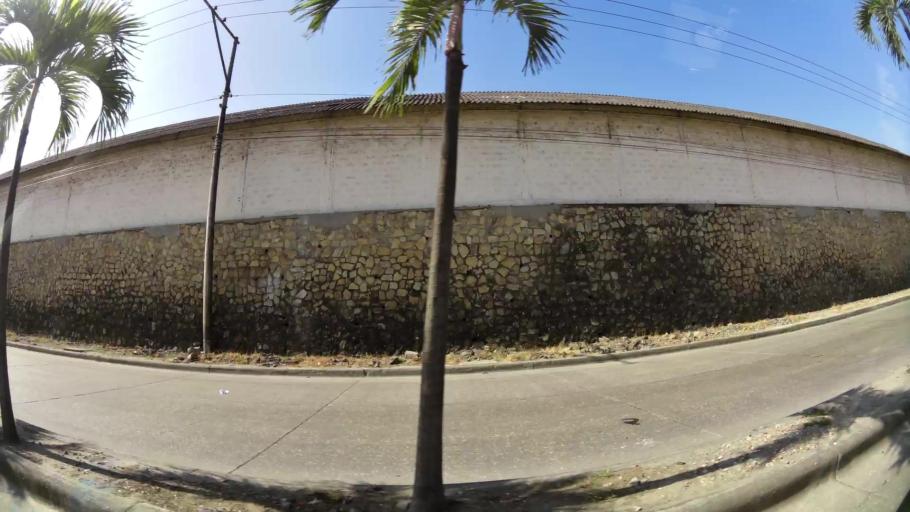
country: EC
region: Guayas
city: Eloy Alfaro
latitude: -2.1014
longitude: -79.9190
